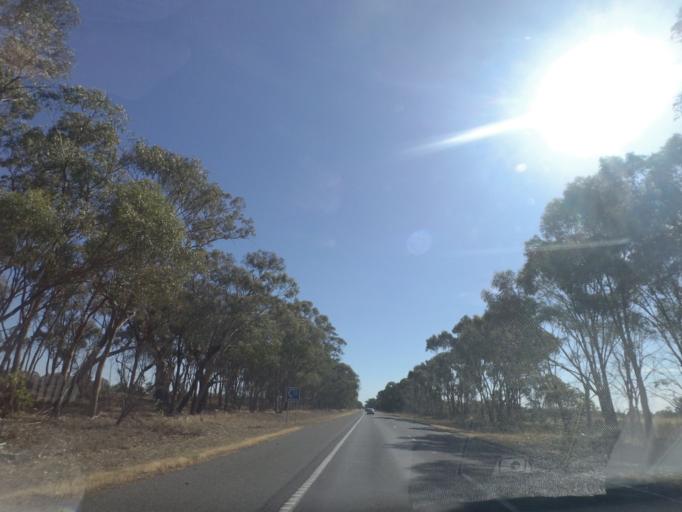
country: AU
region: Victoria
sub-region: Greater Shepparton
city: Shepparton
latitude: -36.6905
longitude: 145.2221
